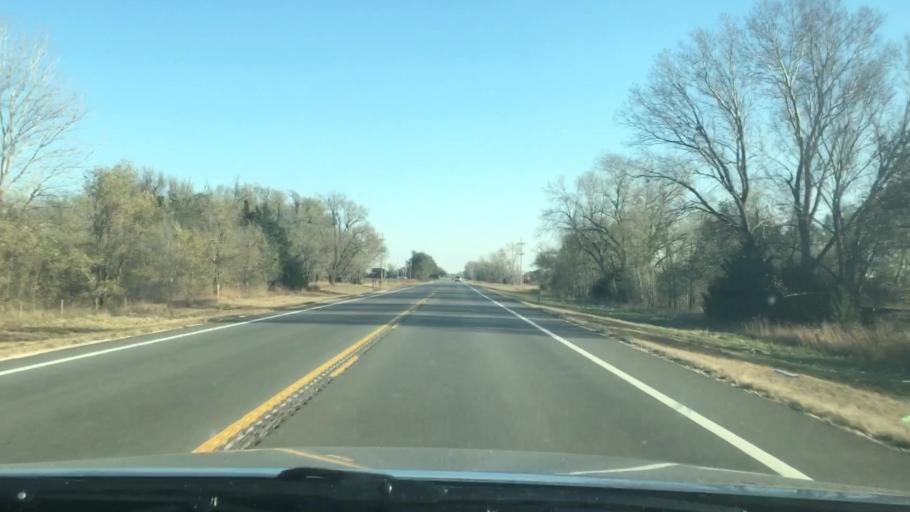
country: US
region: Kansas
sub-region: Reno County
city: Nickerson
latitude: 38.1134
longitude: -98.0340
